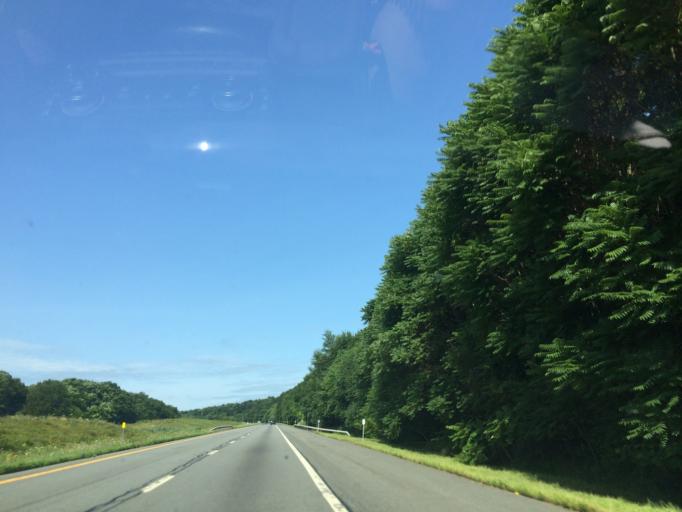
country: US
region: New York
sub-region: Orange County
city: Middletown
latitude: 41.4102
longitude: -74.4428
